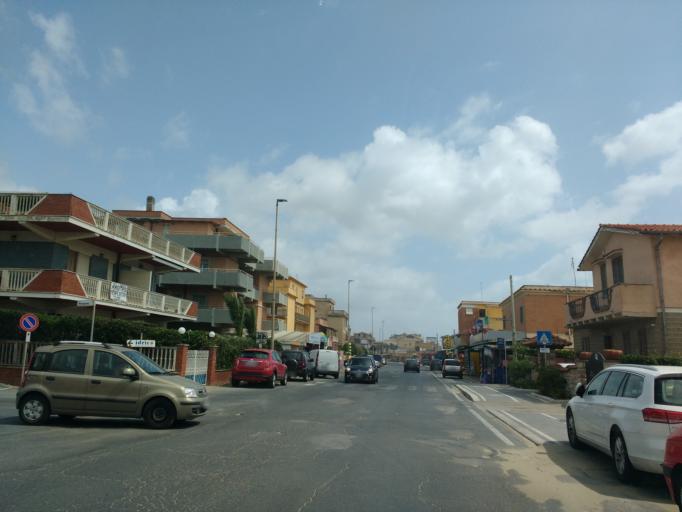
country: IT
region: Latium
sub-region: Citta metropolitana di Roma Capitale
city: Ardea
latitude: 41.5829
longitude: 12.5029
